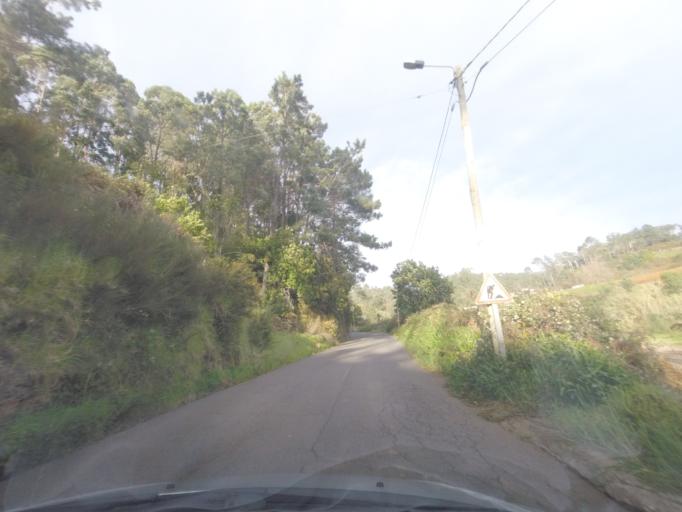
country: PT
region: Madeira
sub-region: Calheta
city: Faja da Ovelha
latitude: 32.7756
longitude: -17.2213
